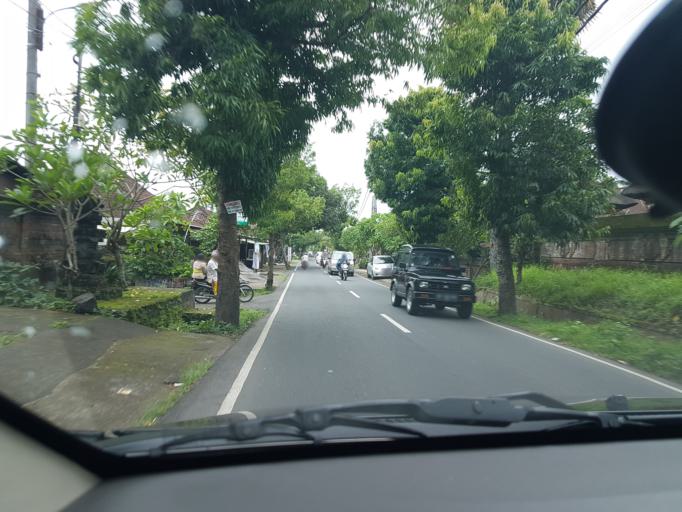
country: ID
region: Bali
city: Banjar Pande
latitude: -8.5094
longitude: 115.2415
